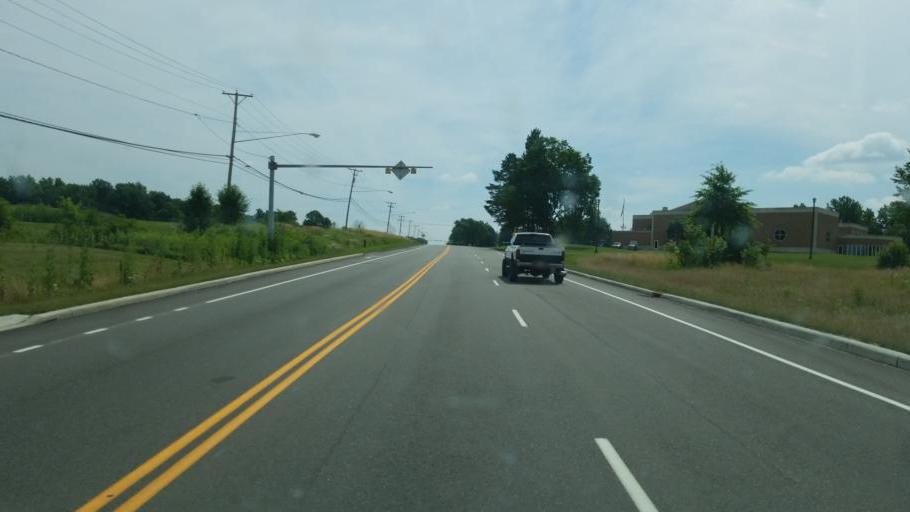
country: US
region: Ohio
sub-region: Summit County
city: Macedonia
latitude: 41.3114
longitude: -81.4876
